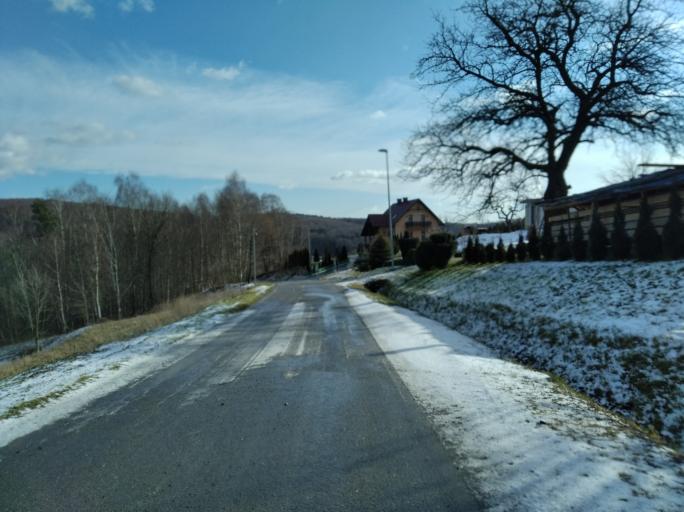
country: PL
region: Subcarpathian Voivodeship
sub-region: Powiat strzyzowski
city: Strzyzow
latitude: 49.8981
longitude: 21.7684
